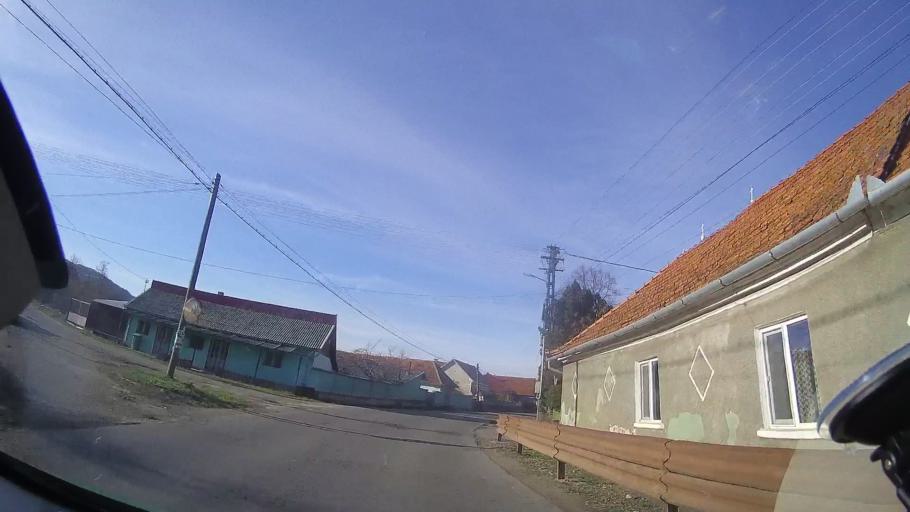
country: RO
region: Bihor
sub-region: Comuna Astileu
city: Astileu
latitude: 47.0284
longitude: 22.3921
